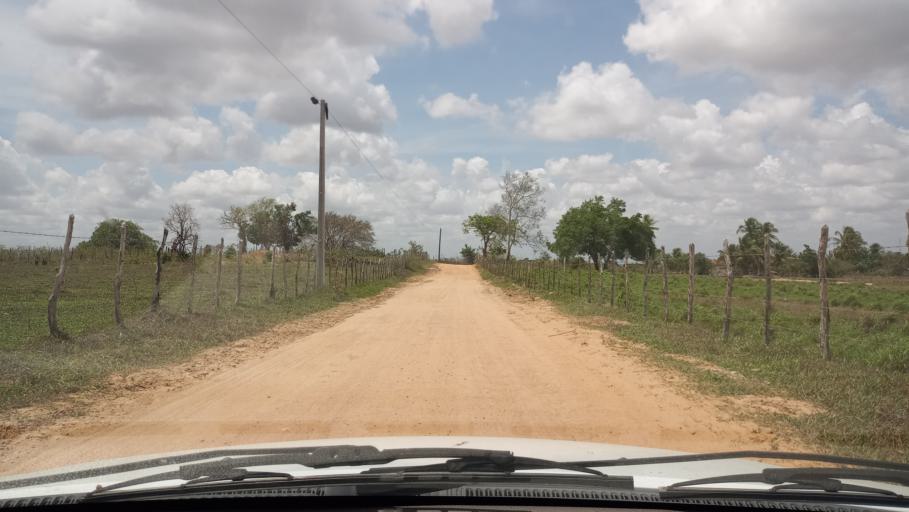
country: BR
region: Rio Grande do Norte
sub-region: Brejinho
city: Brejinho
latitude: -6.2676
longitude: -35.3436
